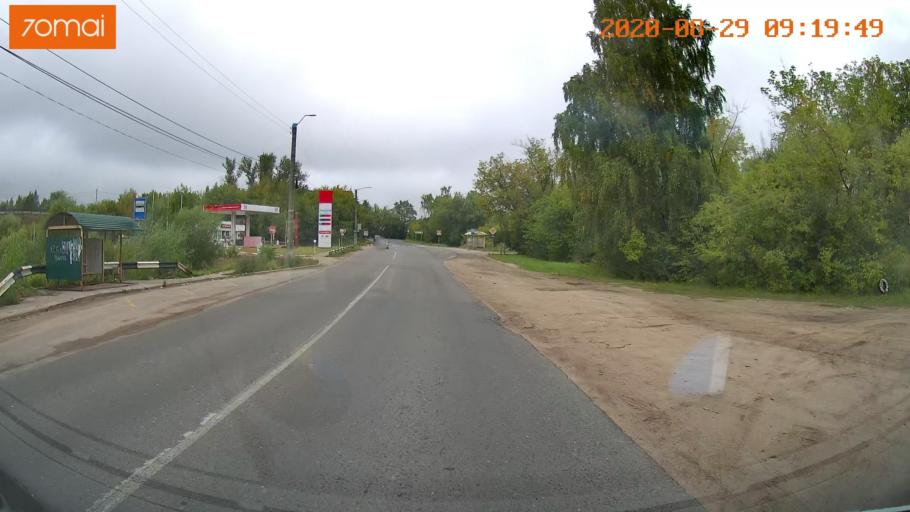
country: RU
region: Ivanovo
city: Kineshma
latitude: 57.4398
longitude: 42.1798
